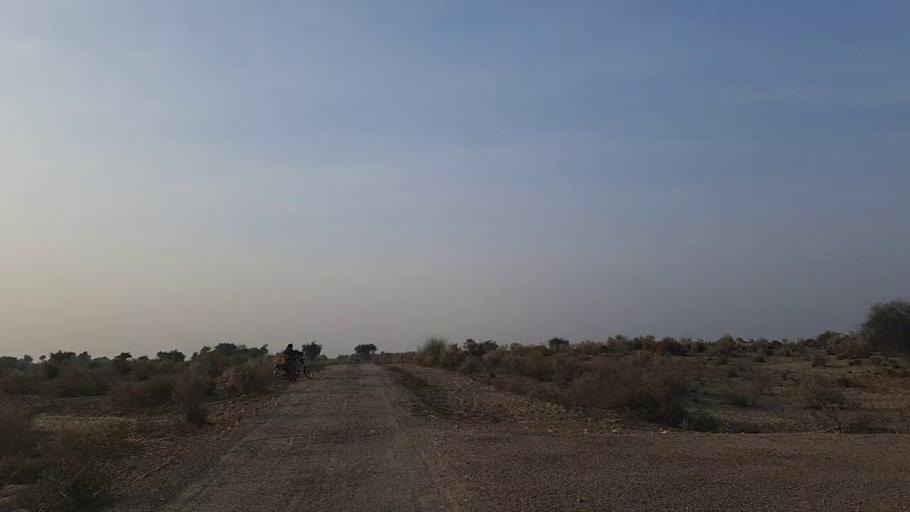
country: PK
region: Sindh
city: Jam Sahib
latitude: 26.4225
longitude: 68.6024
